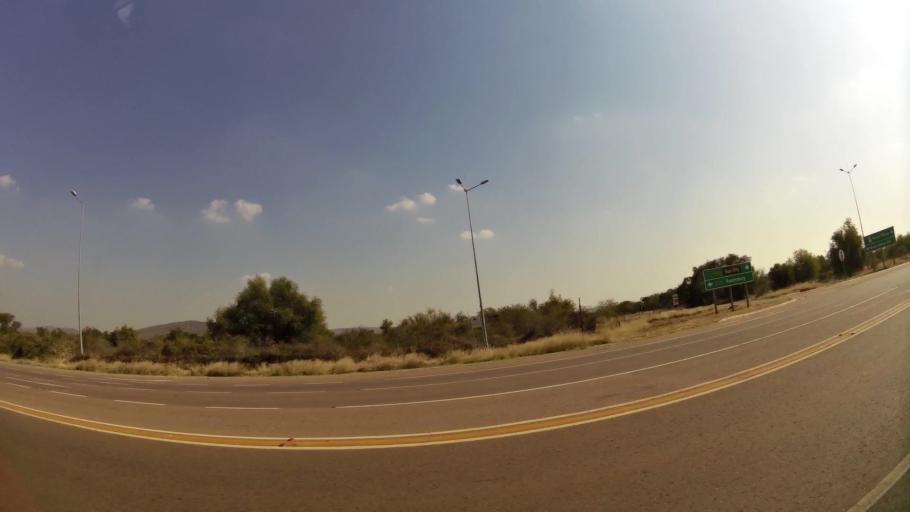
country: ZA
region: North-West
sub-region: Bojanala Platinum District Municipality
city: Mogwase
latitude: -25.4211
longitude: 27.0793
